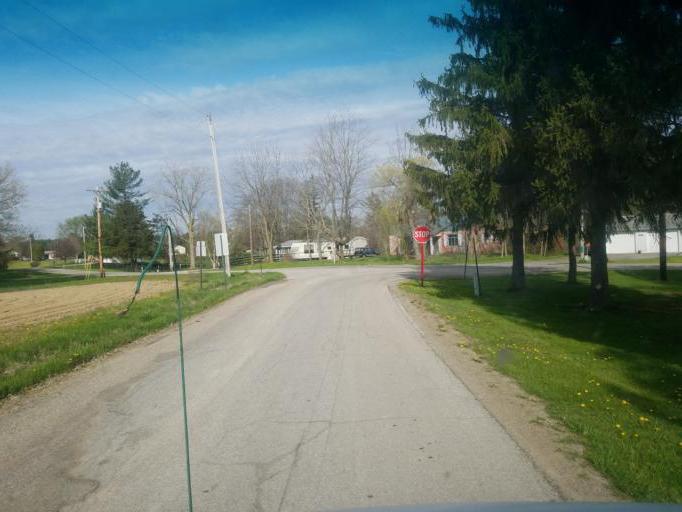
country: US
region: Ohio
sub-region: Delaware County
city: Ashley
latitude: 40.4394
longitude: -82.9700
